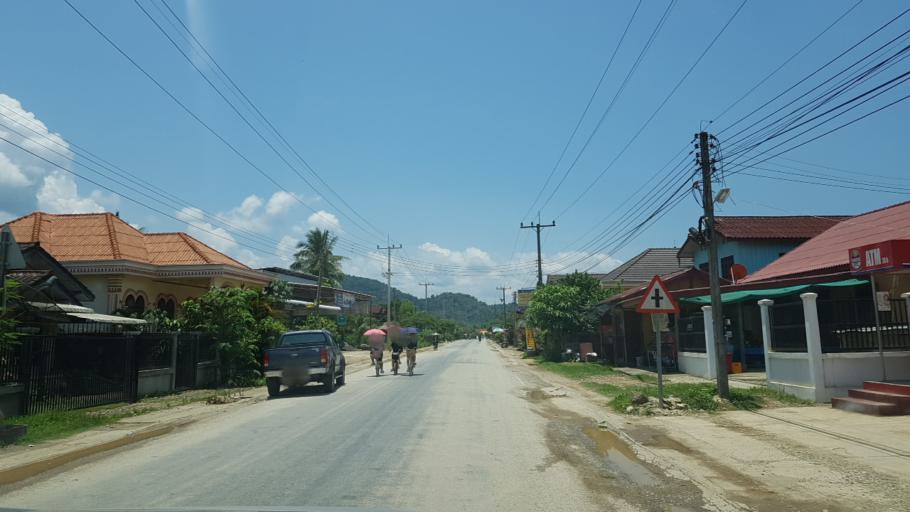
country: LA
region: Vientiane
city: Muang Kasi
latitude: 19.2315
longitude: 102.2529
